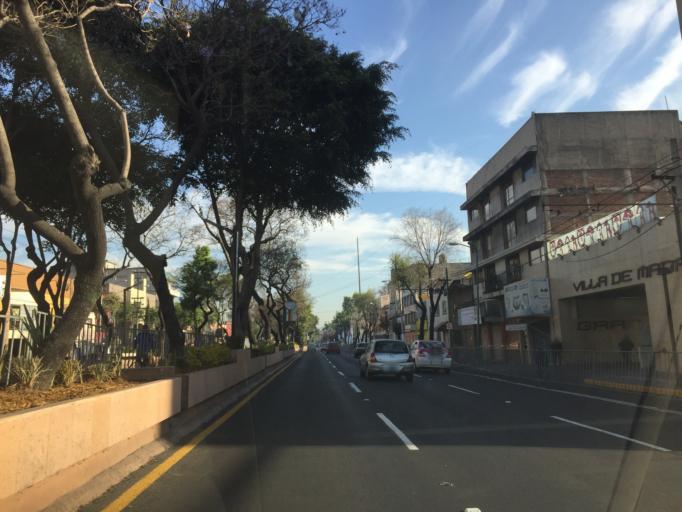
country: MX
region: Mexico City
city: Cuauhtemoc
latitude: 19.4619
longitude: -99.1260
